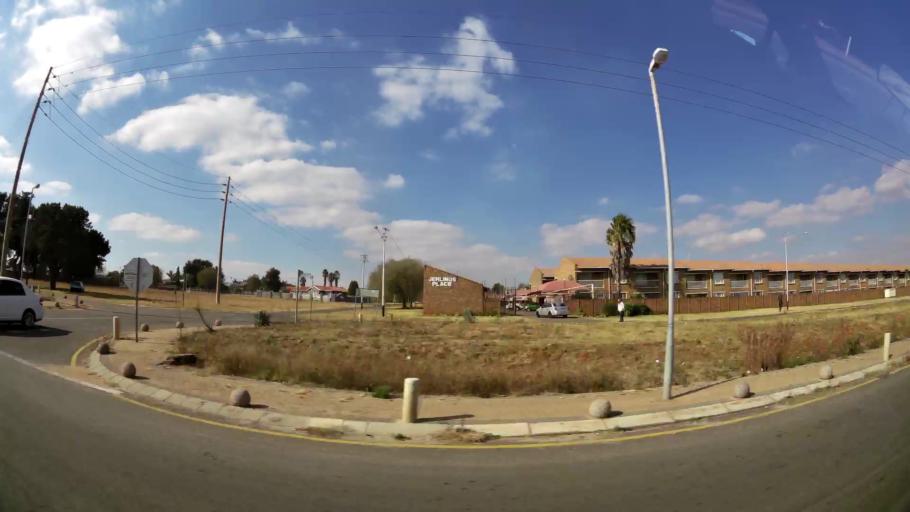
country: ZA
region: Gauteng
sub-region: West Rand District Municipality
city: Krugersdorp
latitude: -26.0862
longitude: 27.7598
